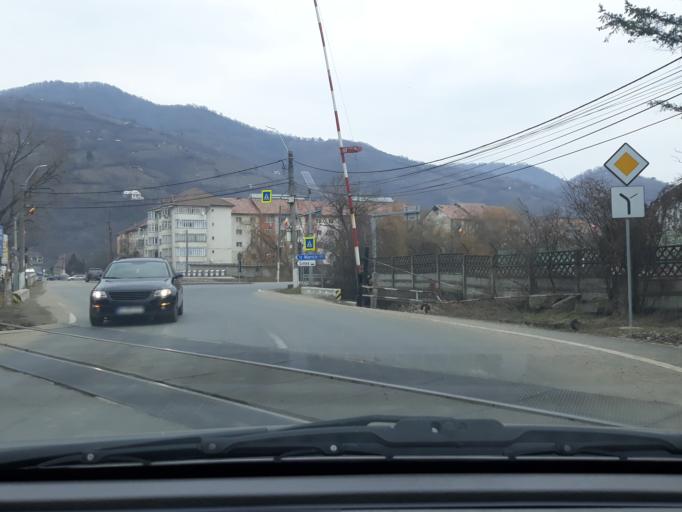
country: RO
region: Salaj
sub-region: Oras Simleu Silvaniei
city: Simleu Silvaniei
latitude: 47.2317
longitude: 22.7837
